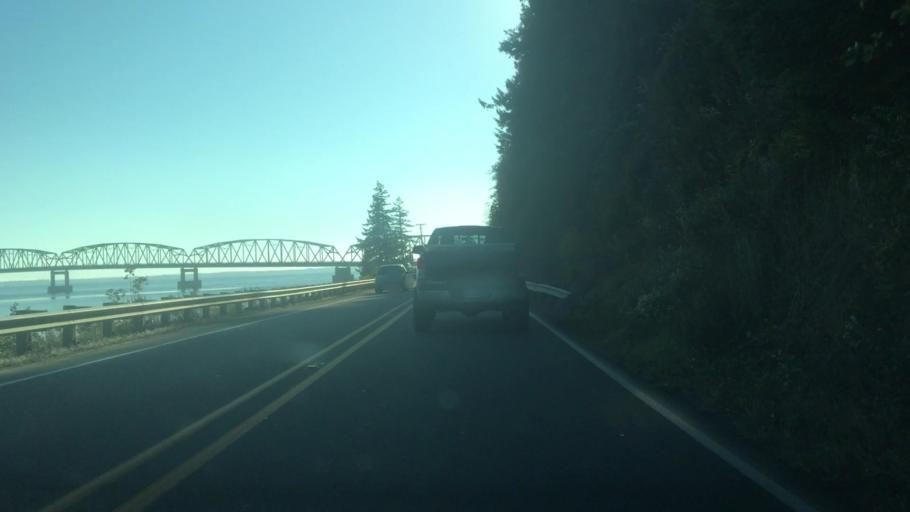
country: US
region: Oregon
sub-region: Clatsop County
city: Astoria
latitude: 46.2430
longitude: -123.8706
